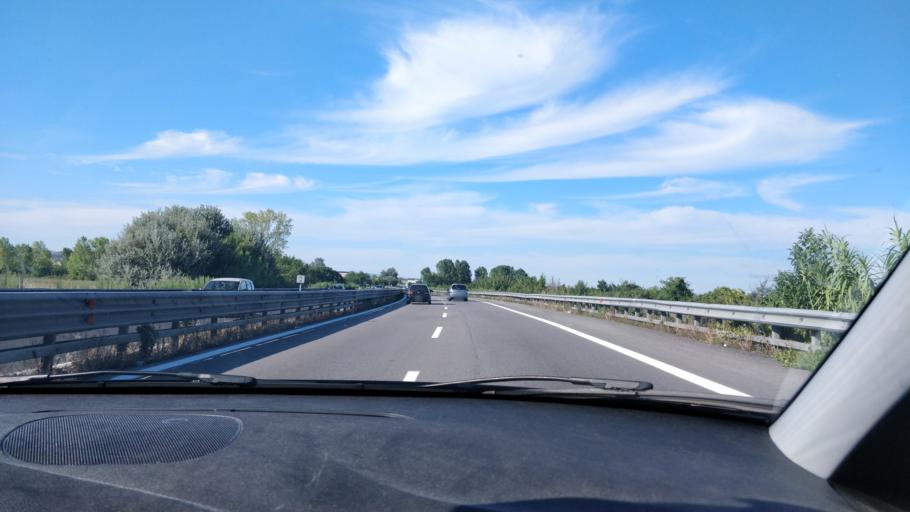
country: IT
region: Abruzzo
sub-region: Provincia di Chieti
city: Sambuceto
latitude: 42.4289
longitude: 14.1775
